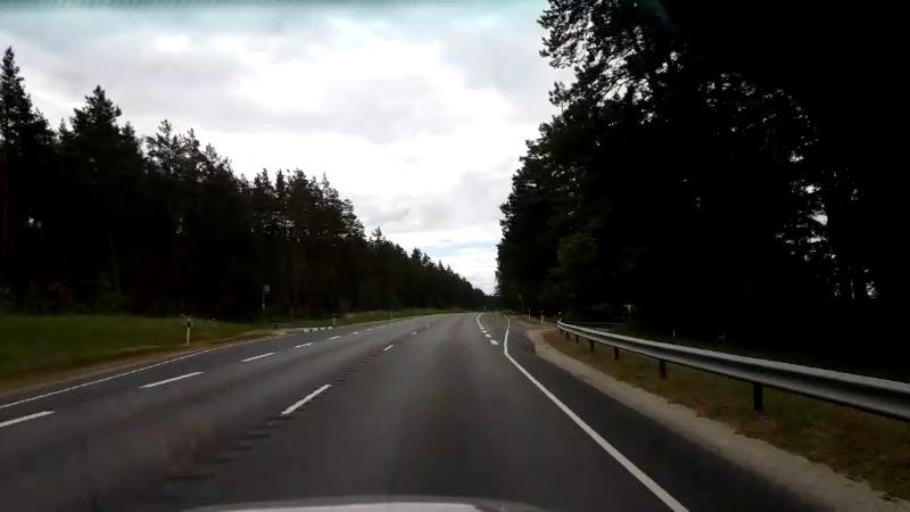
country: EE
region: Paernumaa
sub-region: Paernu linn
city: Parnu
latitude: 58.1611
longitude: 24.4980
